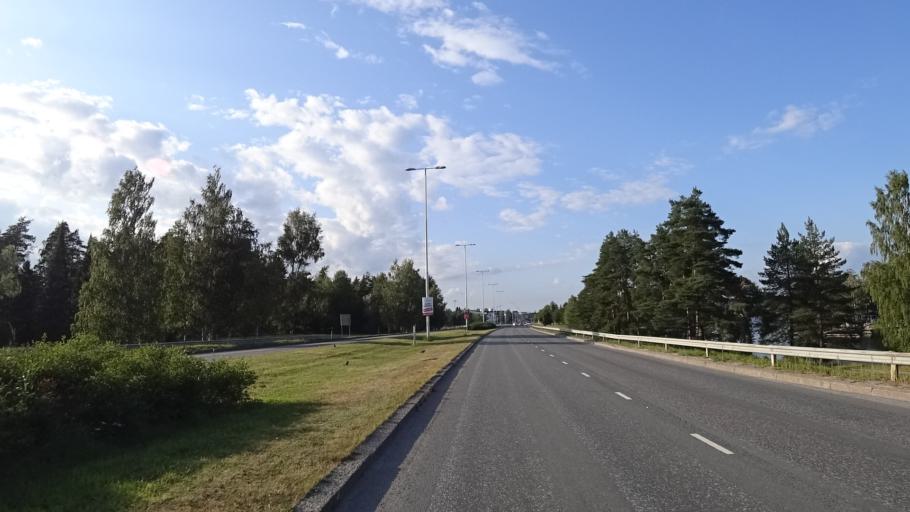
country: FI
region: South Karelia
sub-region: Imatra
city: Imatra
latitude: 61.1860
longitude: 28.7783
